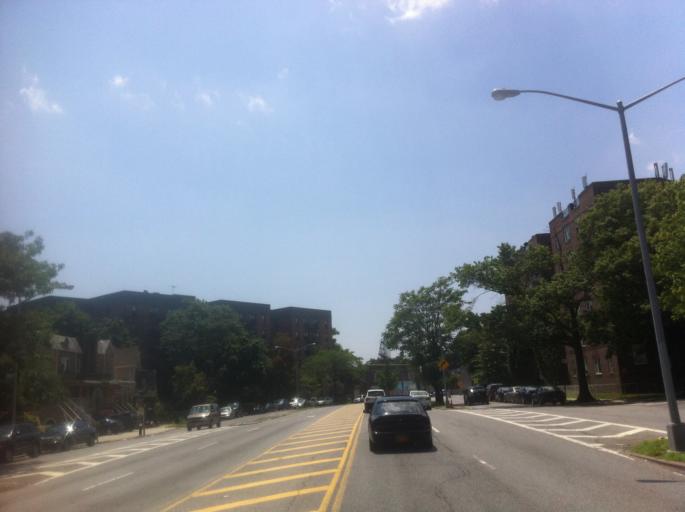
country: US
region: New York
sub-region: Kings County
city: Brooklyn
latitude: 40.6241
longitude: -73.9353
